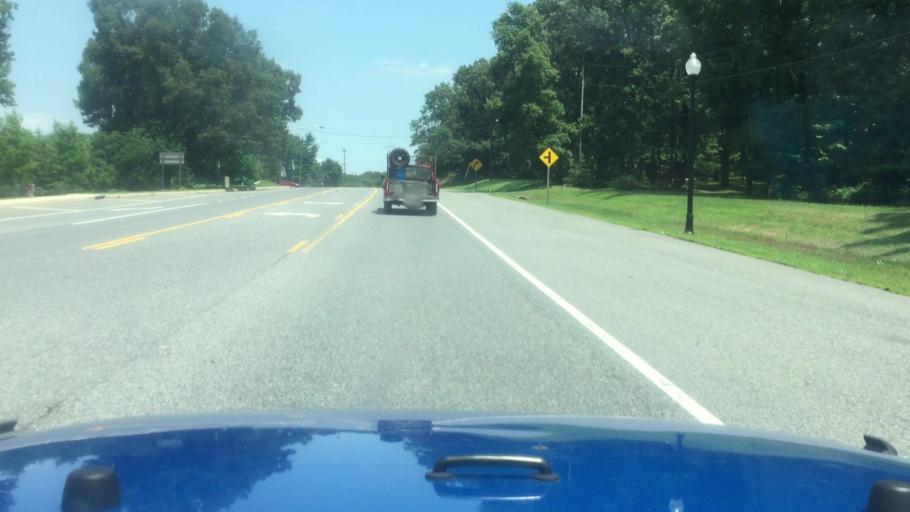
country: US
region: Maryland
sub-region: Anne Arundel County
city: Odenton
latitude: 39.0789
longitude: -76.6833
